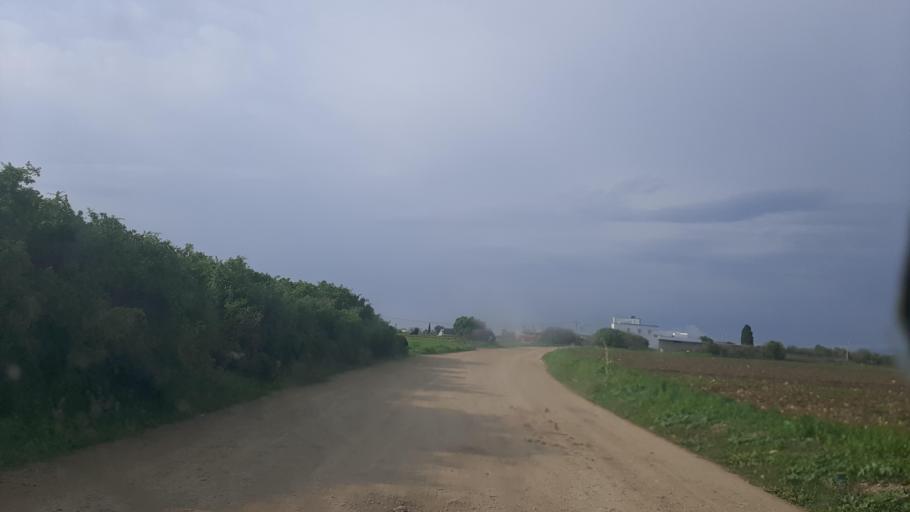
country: TN
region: Nabul
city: Menzel Heurr
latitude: 36.7914
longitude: 10.9649
